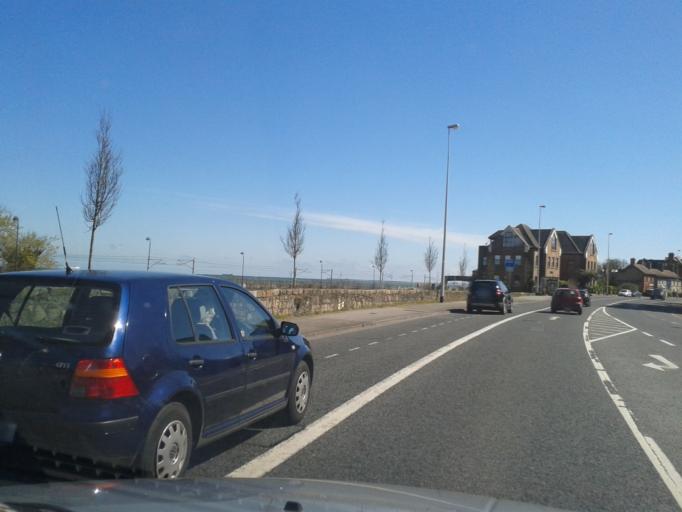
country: IE
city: Booterstown
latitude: 53.3072
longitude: -6.1921
